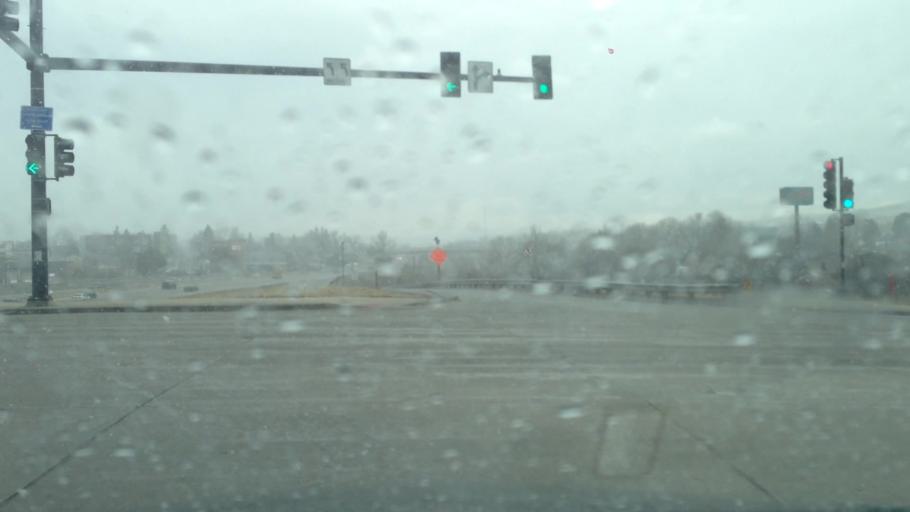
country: US
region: Colorado
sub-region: Douglas County
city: Castle Rock
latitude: 39.3803
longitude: -104.8614
